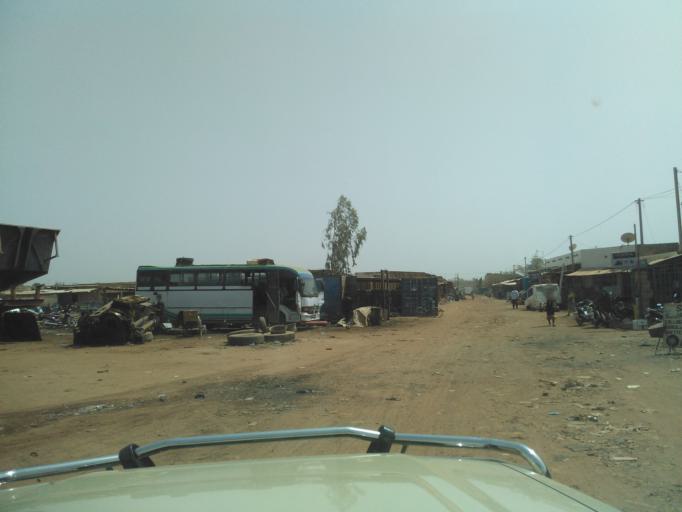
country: BF
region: Centre
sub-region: Kadiogo Province
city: Ouagadougou
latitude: 12.3903
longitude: -1.5665
